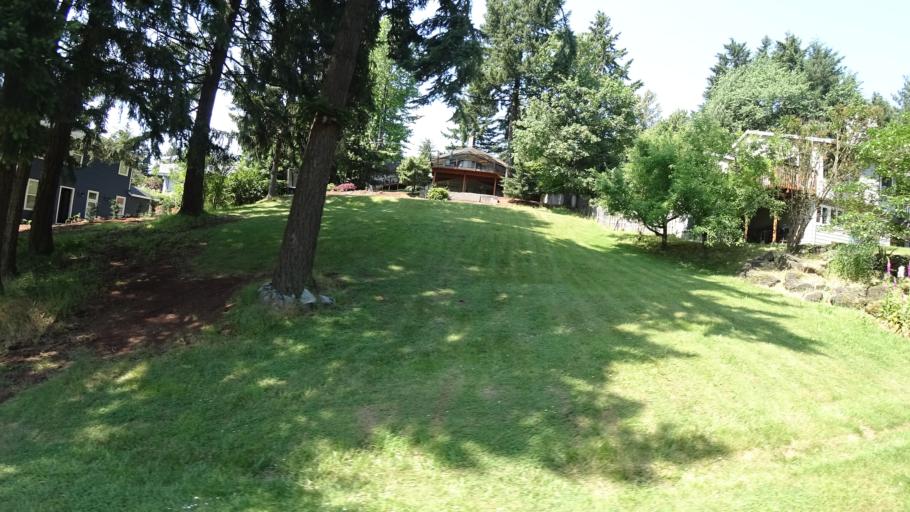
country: US
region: Oregon
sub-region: Clackamas County
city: Happy Valley
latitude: 45.4427
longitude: -122.5552
